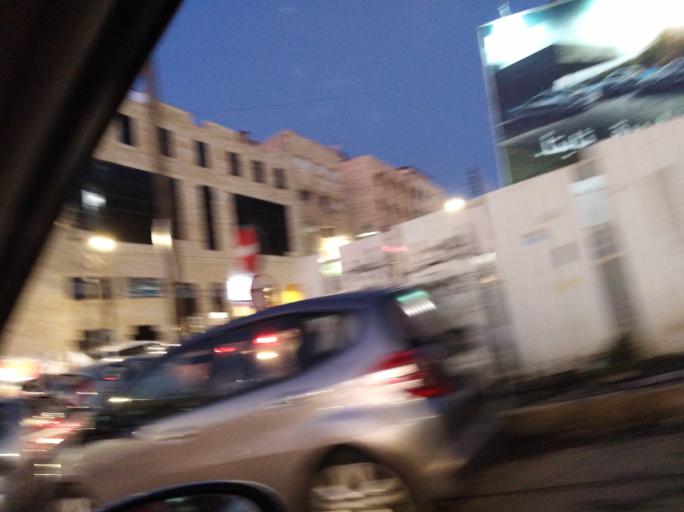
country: JO
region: Amman
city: Wadi as Sir
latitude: 31.9579
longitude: 35.8652
